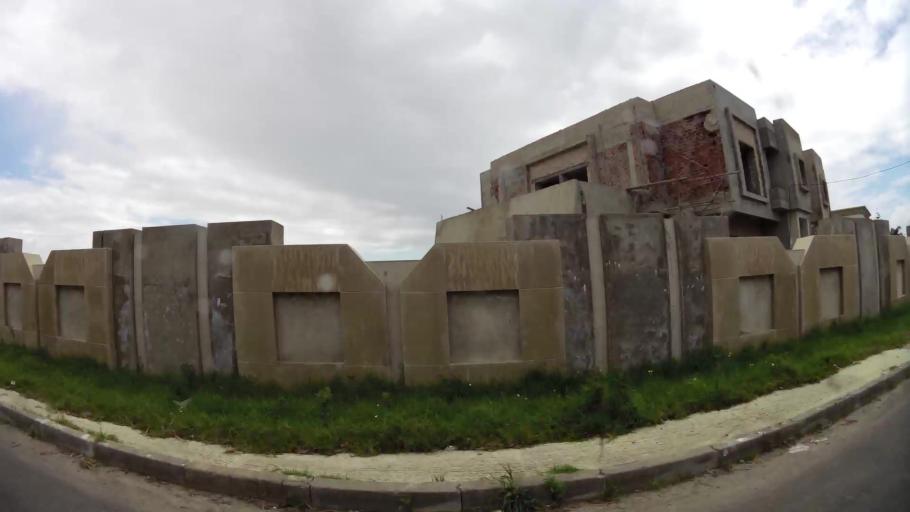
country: MA
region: Tanger-Tetouan
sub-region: Tanger-Assilah
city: Tangier
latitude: 35.7802
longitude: -5.8598
